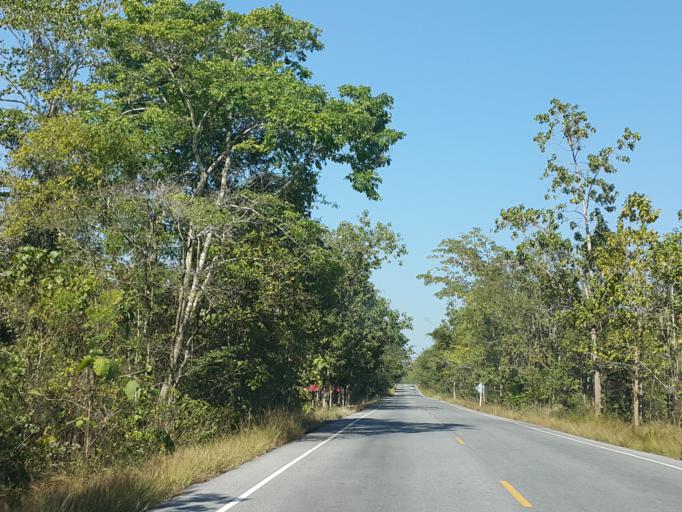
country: TH
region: Sukhothai
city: Thung Saliam
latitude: 17.4204
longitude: 99.3823
